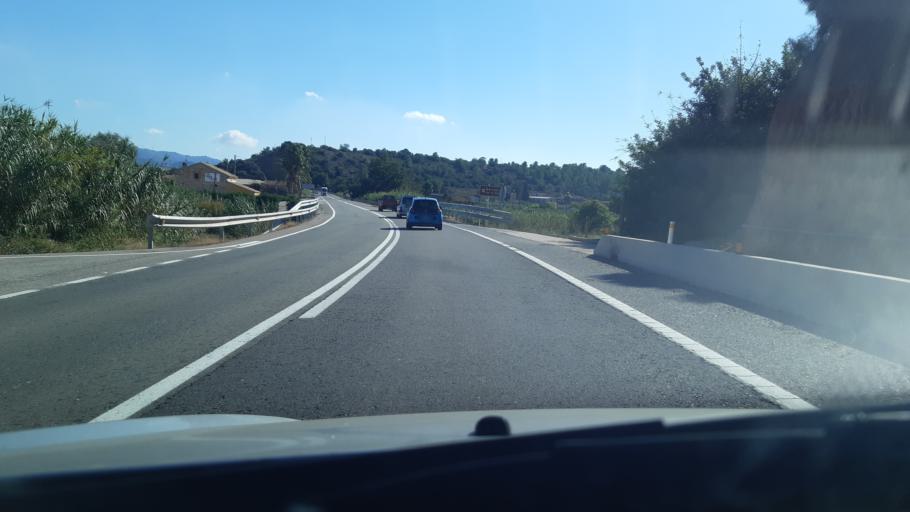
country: ES
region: Catalonia
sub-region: Provincia de Tarragona
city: Tivenys
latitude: 40.8856
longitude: 0.4921
